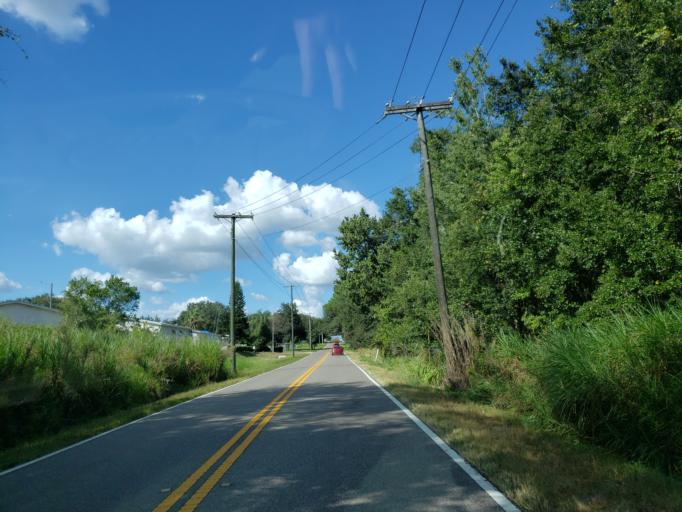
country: US
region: Florida
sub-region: Hillsborough County
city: Valrico
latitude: 27.9313
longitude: -82.2196
